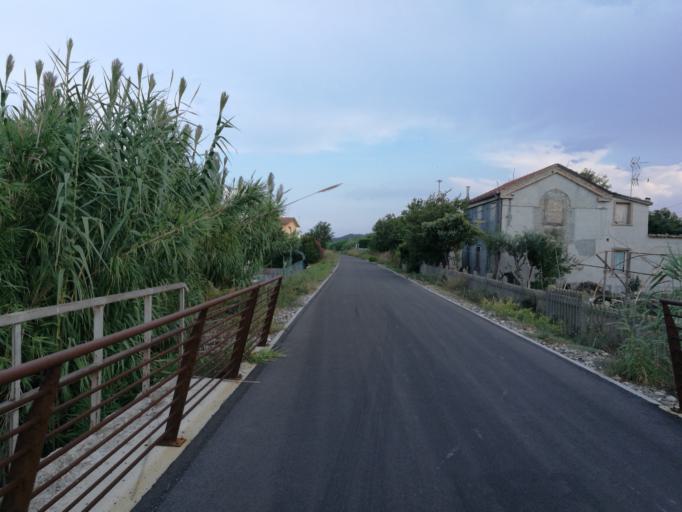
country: IT
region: Abruzzo
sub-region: Provincia di Chieti
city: Fossacesia
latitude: 42.2458
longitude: 14.5172
